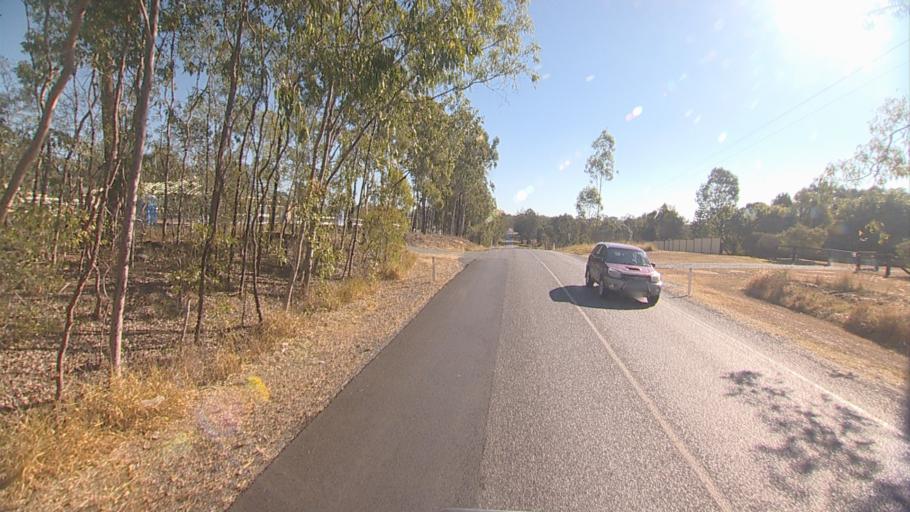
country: AU
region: Queensland
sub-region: Logan
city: North Maclean
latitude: -27.7926
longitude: 153.0257
